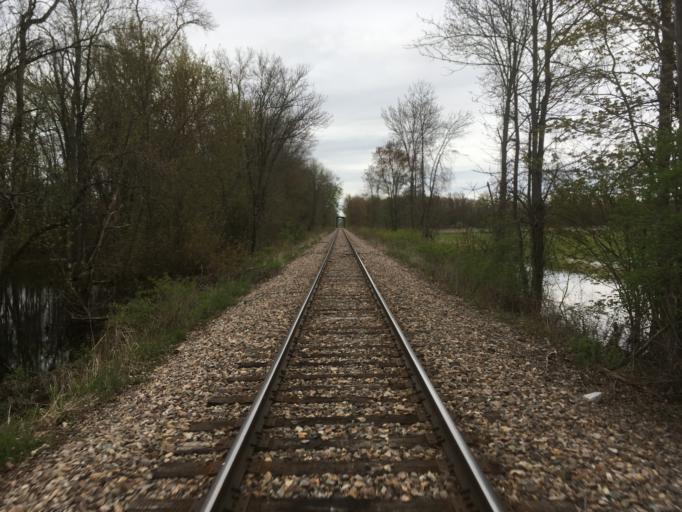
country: US
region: Vermont
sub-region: Addison County
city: Middlebury (village)
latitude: 43.9516
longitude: -73.1620
